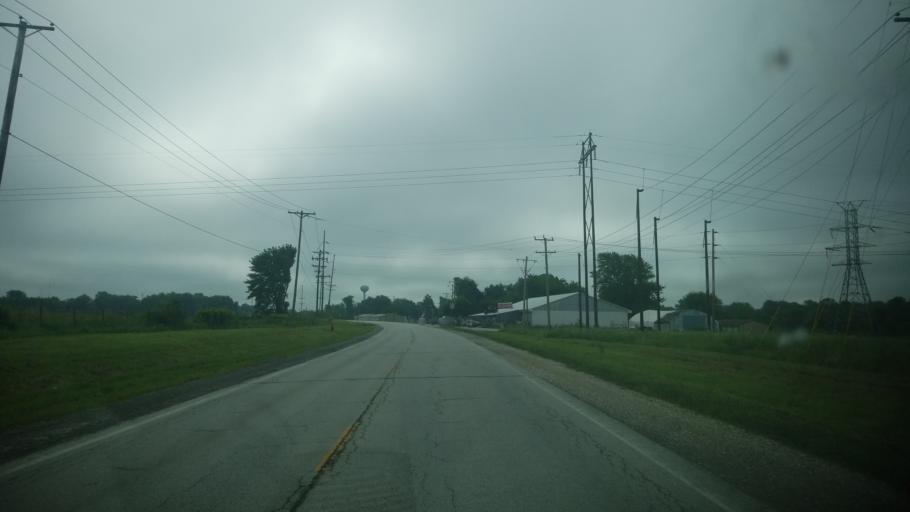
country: US
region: Missouri
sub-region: Pike County
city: Bowling Green
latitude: 39.3444
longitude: -91.2198
